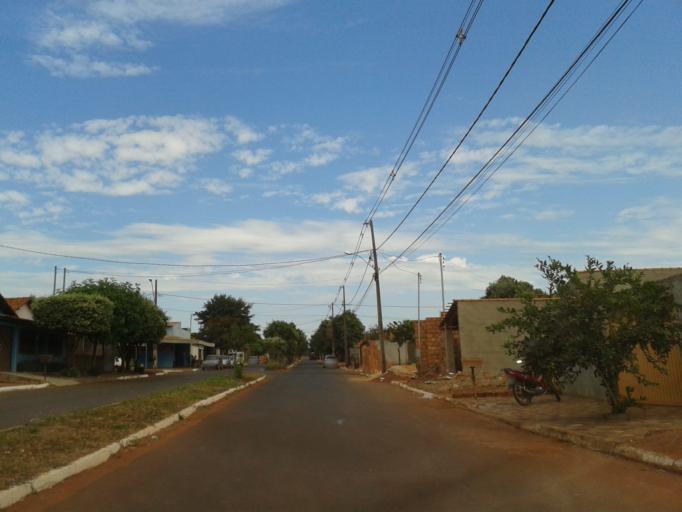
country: BR
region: Minas Gerais
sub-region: Santa Vitoria
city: Santa Vitoria
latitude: -18.8521
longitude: -50.1347
